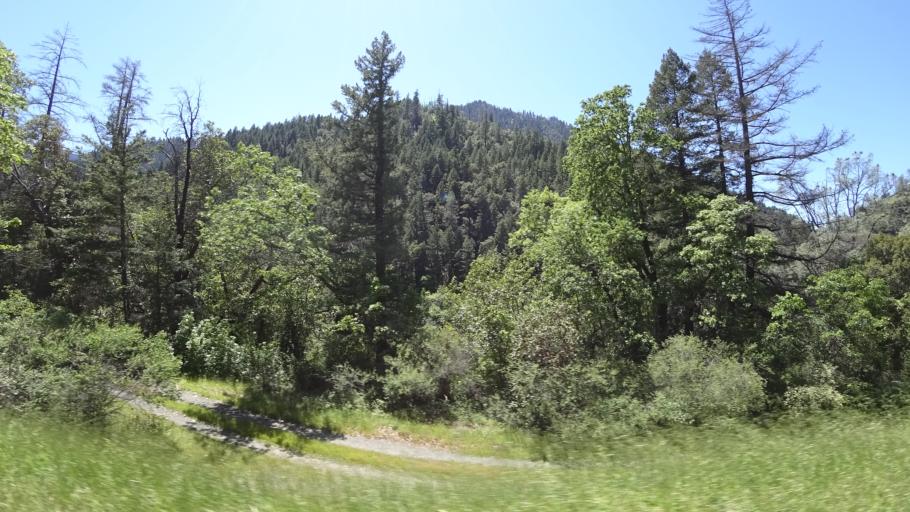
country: US
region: California
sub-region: Trinity County
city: Hayfork
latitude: 40.7920
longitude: -123.3507
